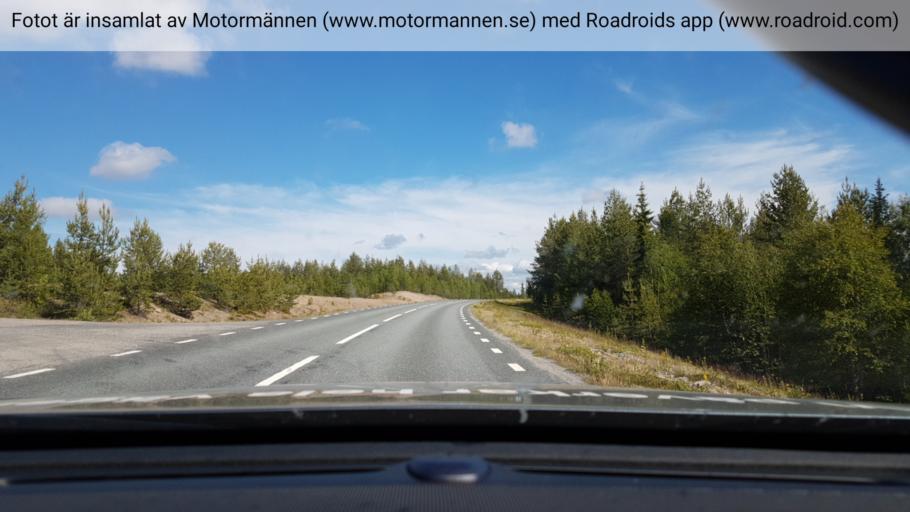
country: SE
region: Vaesterbotten
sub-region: Sorsele Kommun
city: Sorsele
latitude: 65.5592
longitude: 17.9124
